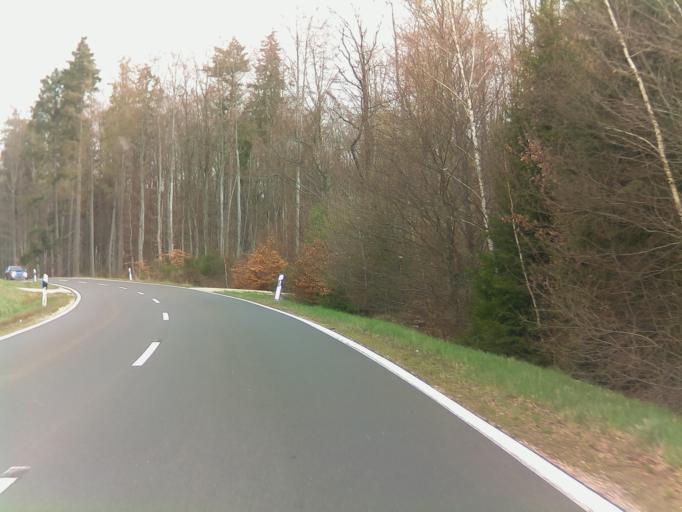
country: DE
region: Rheinland-Pfalz
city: Asbach
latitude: 49.8314
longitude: 7.2747
